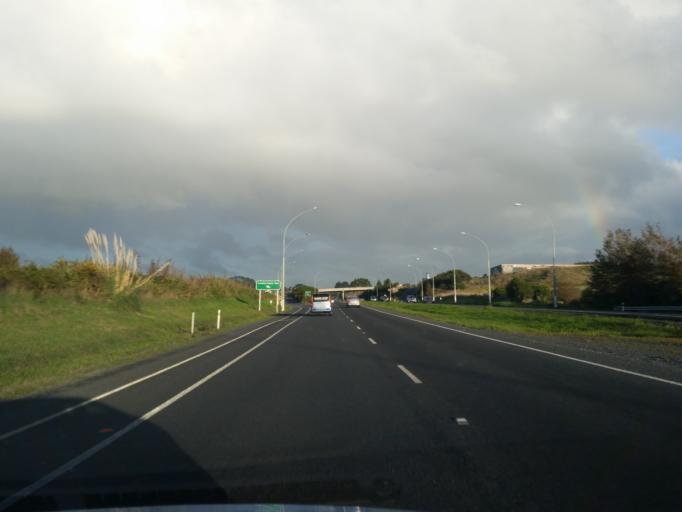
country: NZ
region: Waikato
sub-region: Waikato District
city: Te Kauwhata
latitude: -37.3513
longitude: 175.0799
